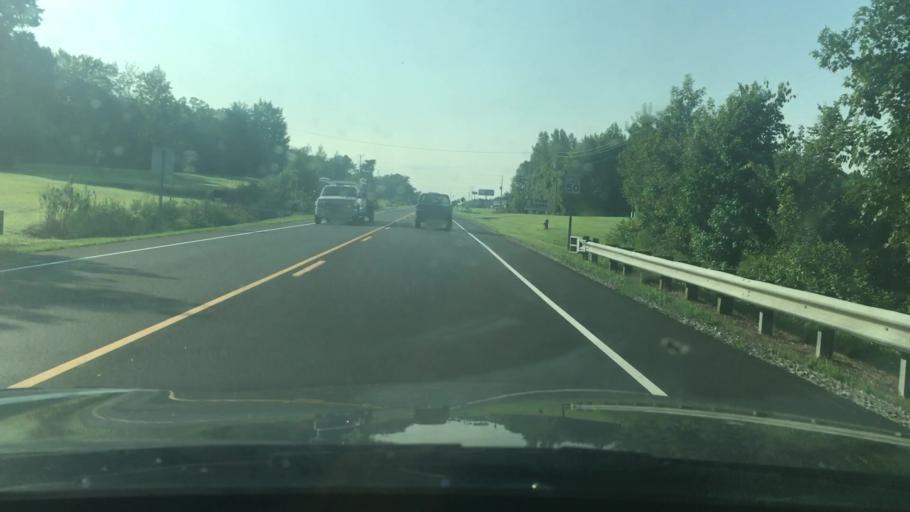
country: US
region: North Carolina
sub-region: Caswell County
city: Yanceyville
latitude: 36.4224
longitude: -79.3545
